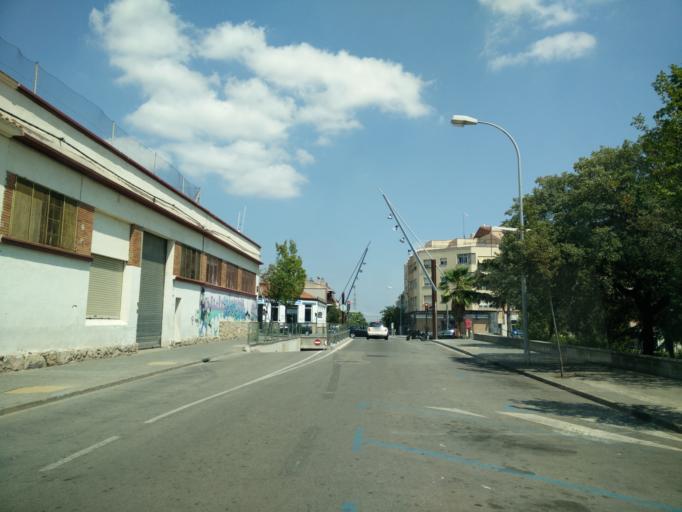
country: ES
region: Catalonia
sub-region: Provincia de Barcelona
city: Terrassa
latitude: 41.5670
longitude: 2.0257
